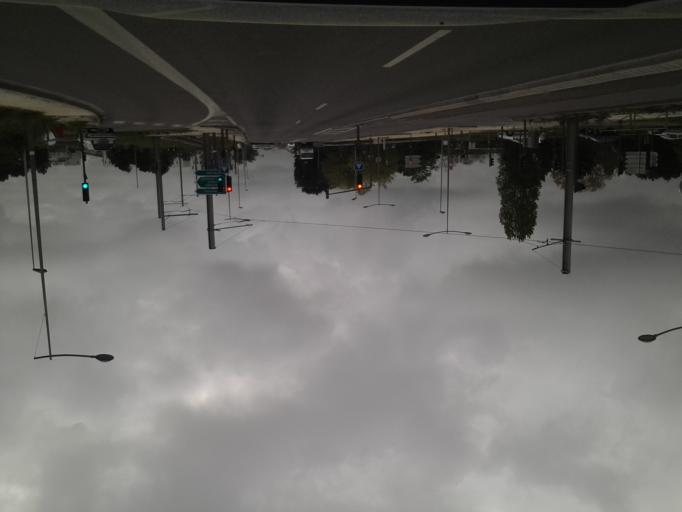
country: FR
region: Aquitaine
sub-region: Departement de la Gironde
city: Le Haillan
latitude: 44.8580
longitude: -0.6644
